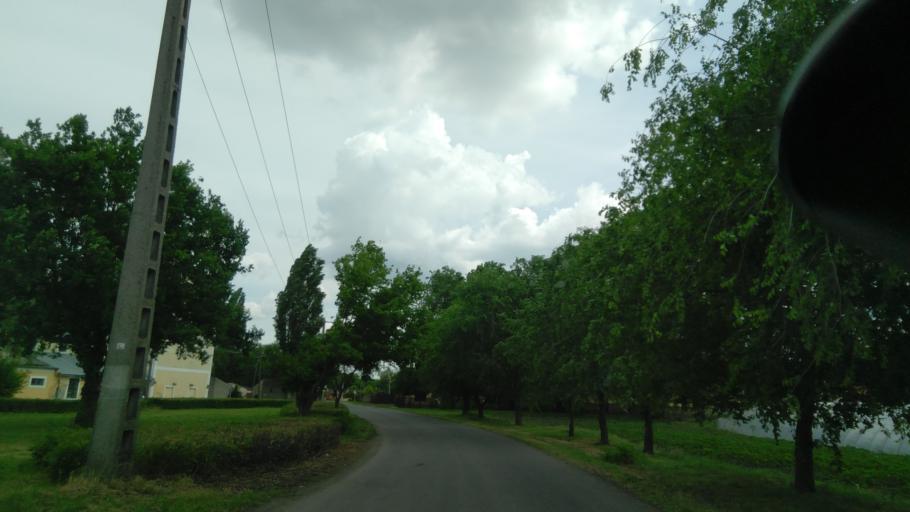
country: HU
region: Bekes
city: Mezohegyes
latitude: 46.3155
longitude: 20.8216
